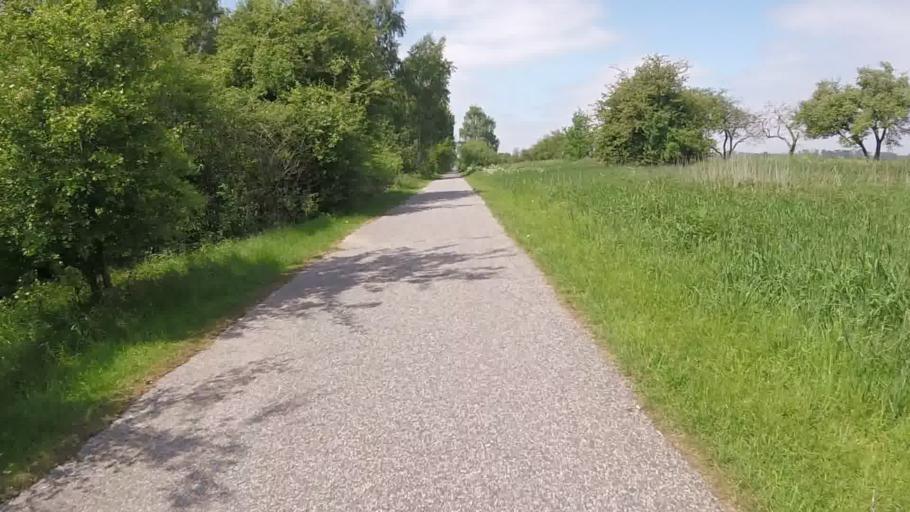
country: DE
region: Schleswig-Holstein
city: Oststeinbek
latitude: 53.4897
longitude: 10.1689
